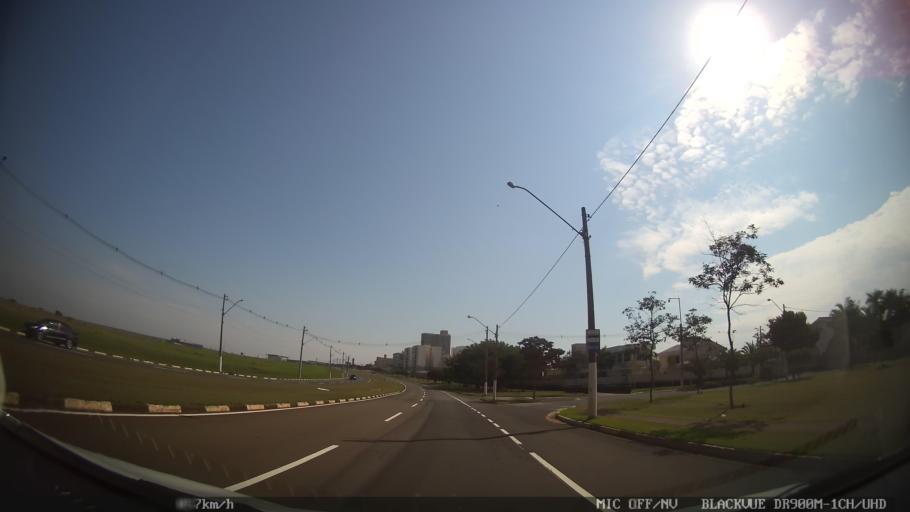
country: BR
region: Sao Paulo
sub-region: Paulinia
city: Paulinia
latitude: -22.7847
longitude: -47.1480
